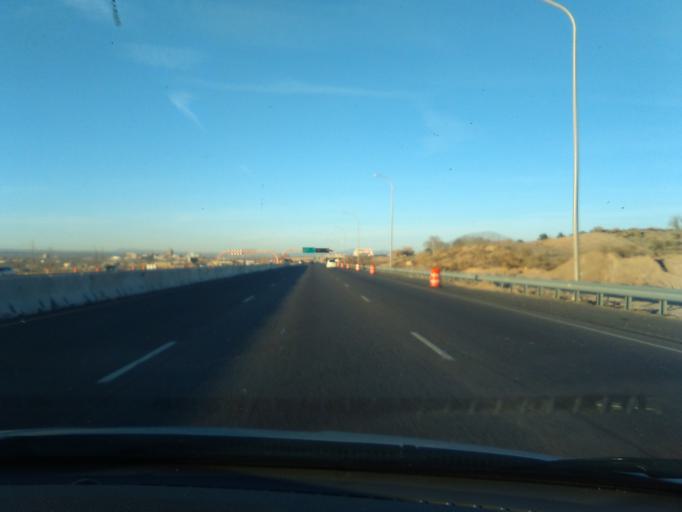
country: US
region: New Mexico
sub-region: Bernalillo County
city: South Valley
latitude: 35.0342
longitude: -106.6379
